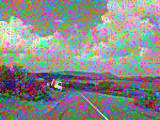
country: IE
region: Ulster
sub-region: County Donegal
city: Ramelton
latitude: 55.1848
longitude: -7.6017
